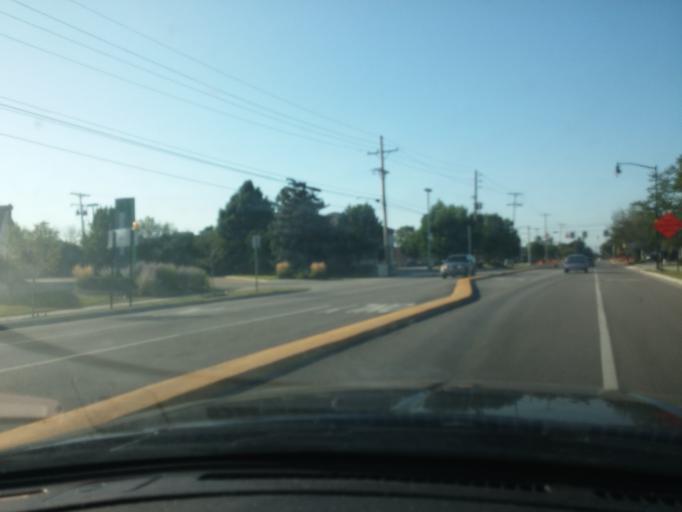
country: US
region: Indiana
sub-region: Tippecanoe County
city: West Lafayette
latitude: 40.4520
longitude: -86.9157
